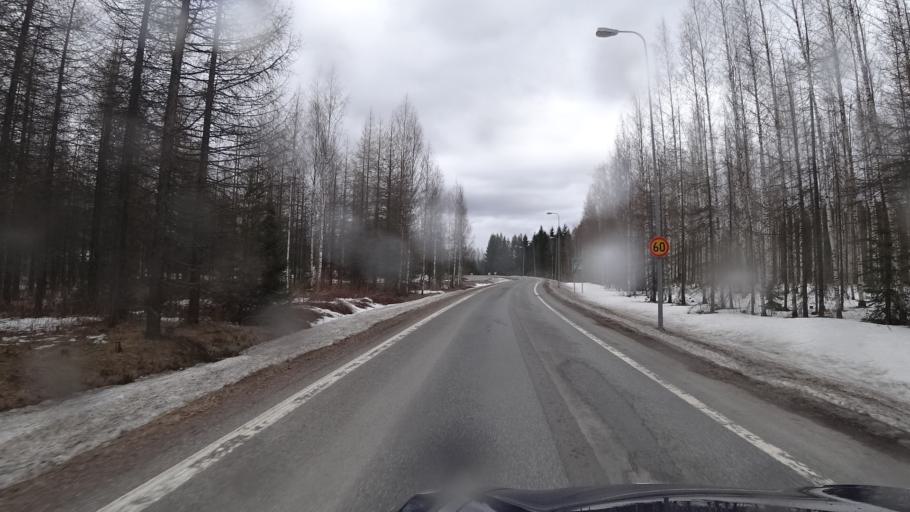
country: FI
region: Paijanne Tavastia
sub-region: Lahti
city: Nastola
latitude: 60.9214
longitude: 25.9955
